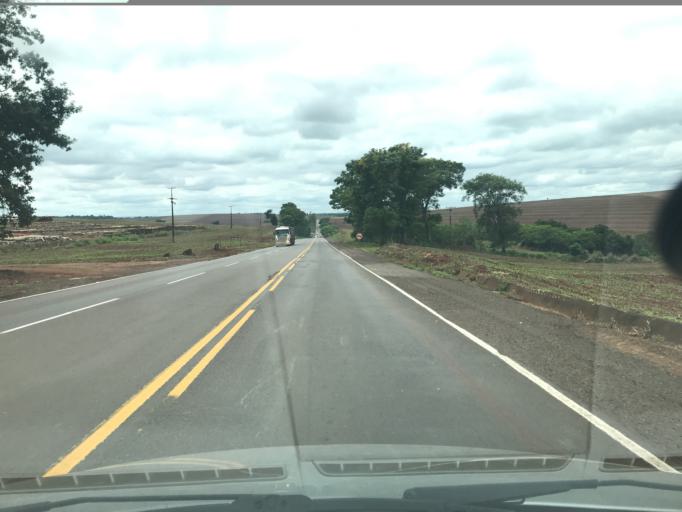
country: BR
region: Parana
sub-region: Terra Boa
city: Terra Boa
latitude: -23.6002
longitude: -52.3986
